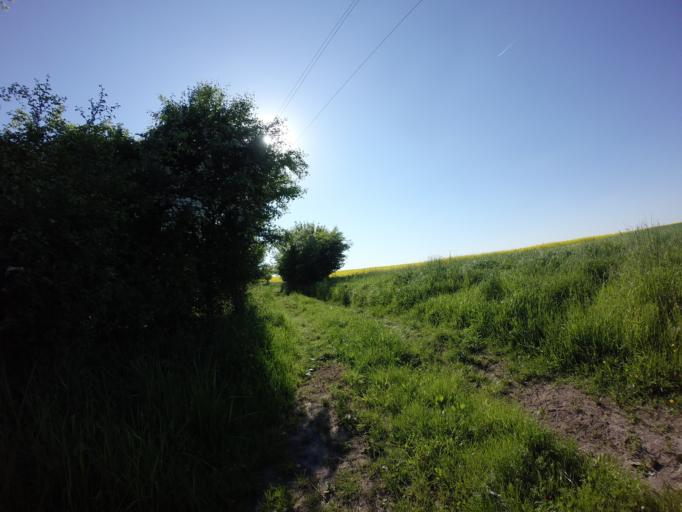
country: PL
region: West Pomeranian Voivodeship
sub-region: Powiat choszczenski
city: Choszczno
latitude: 53.1369
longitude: 15.3953
